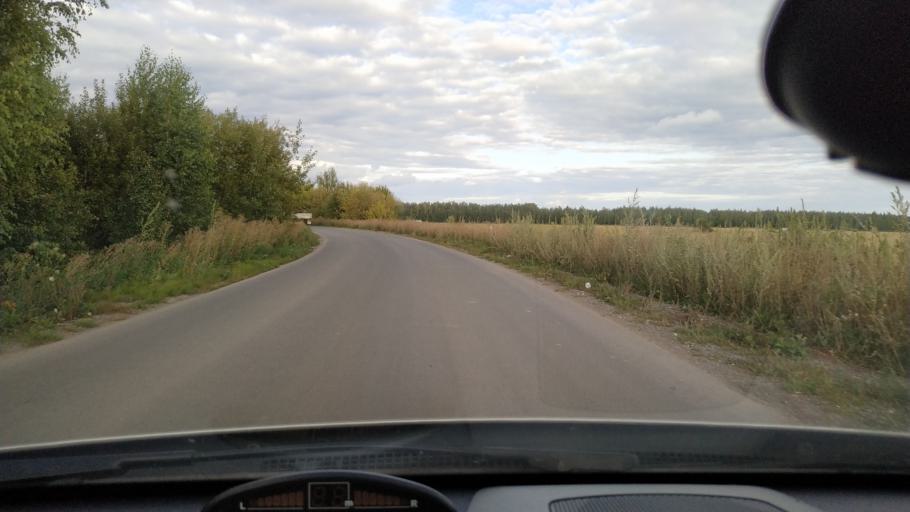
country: RU
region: Rjazan
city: Polyany
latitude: 54.5767
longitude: 39.8544
